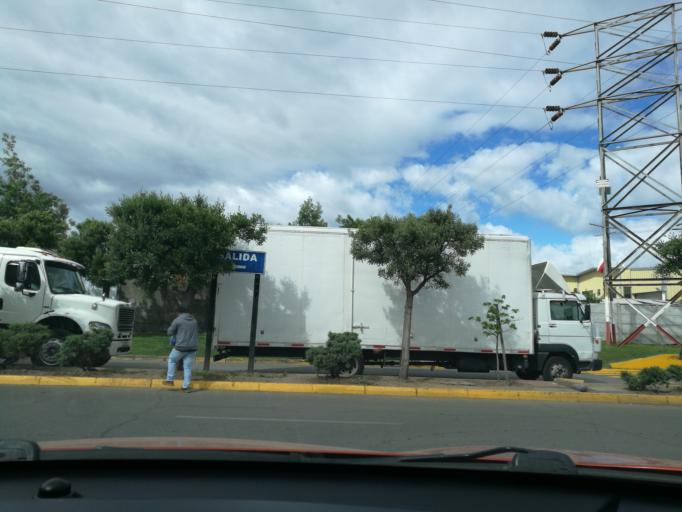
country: CL
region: O'Higgins
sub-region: Provincia de Cachapoal
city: Rancagua
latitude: -34.1807
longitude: -70.7313
